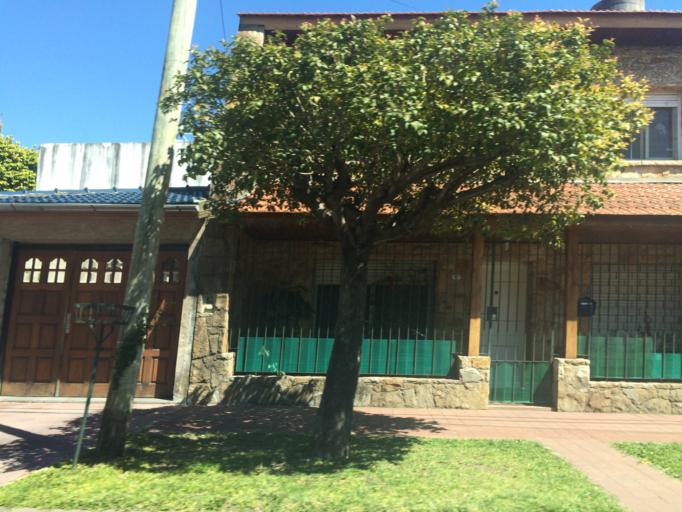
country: AR
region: Buenos Aires
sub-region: Partido de Lanus
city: Lanus
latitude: -34.7189
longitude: -58.3985
